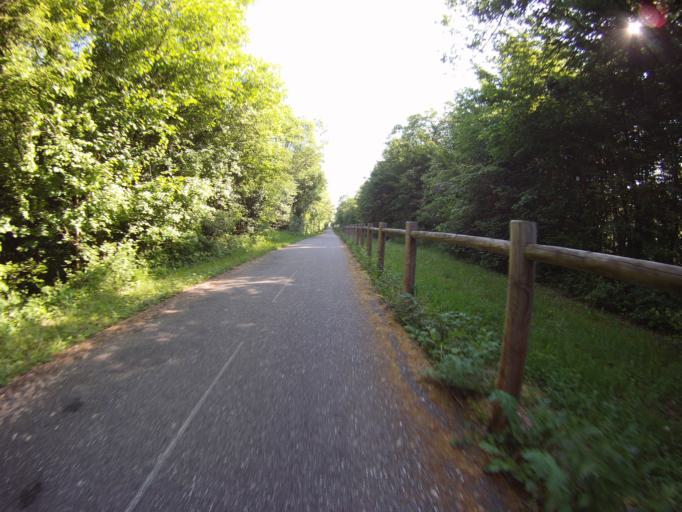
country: FR
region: Lorraine
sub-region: Departement de Meurthe-et-Moselle
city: Champenoux
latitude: 48.7432
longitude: 6.3180
